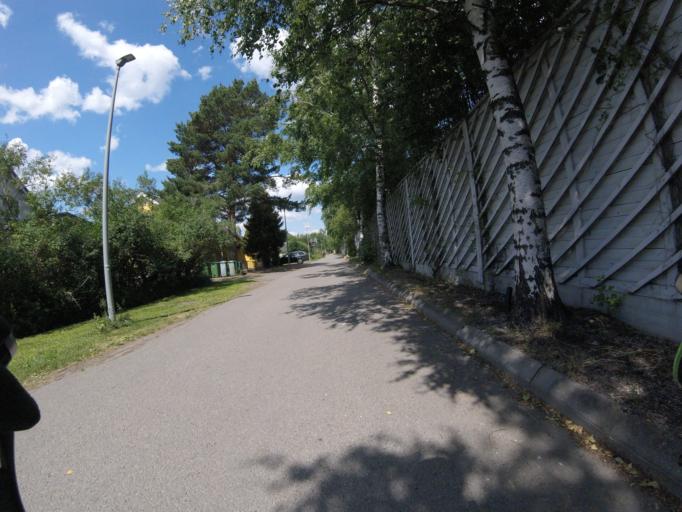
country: NO
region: Akershus
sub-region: Skedsmo
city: Lillestrom
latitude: 59.9592
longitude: 11.0664
